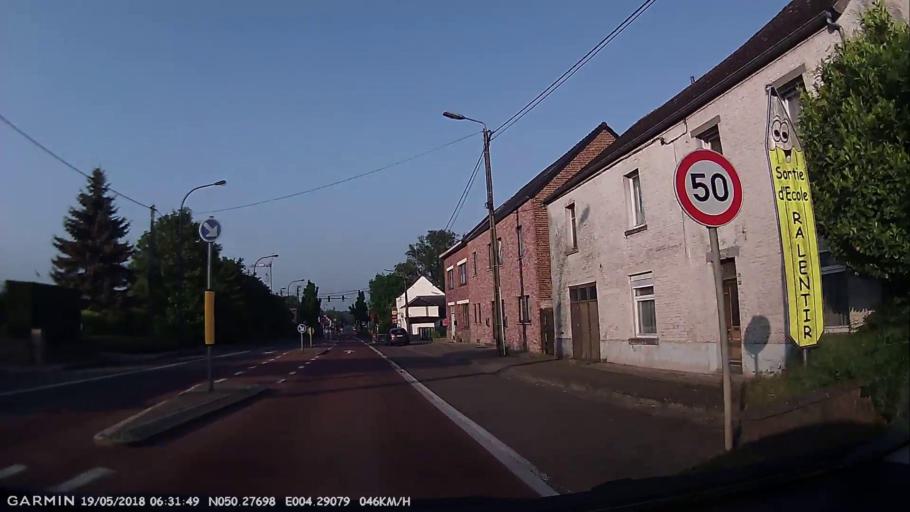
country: BE
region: Wallonia
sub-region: Province du Hainaut
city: Thuin
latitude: 50.2769
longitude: 4.2907
